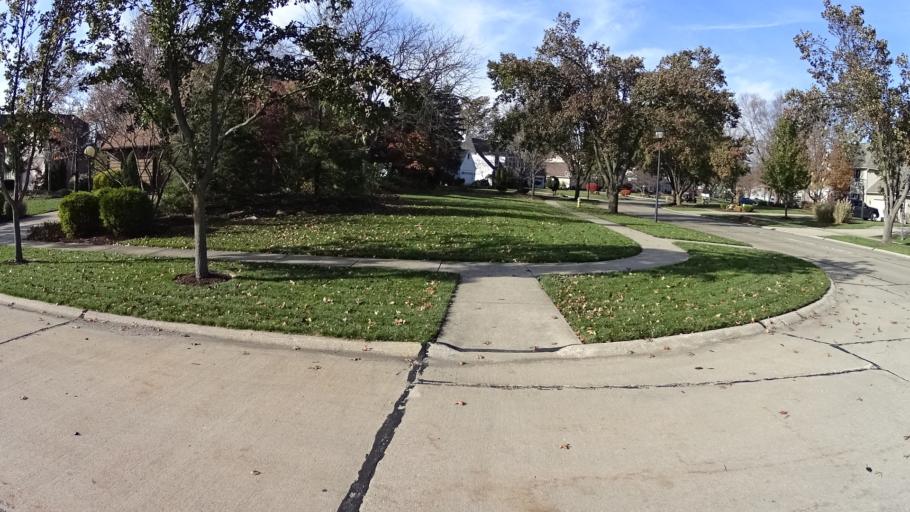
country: US
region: Ohio
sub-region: Lorain County
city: Avon Lake
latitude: 41.4957
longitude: -81.9816
